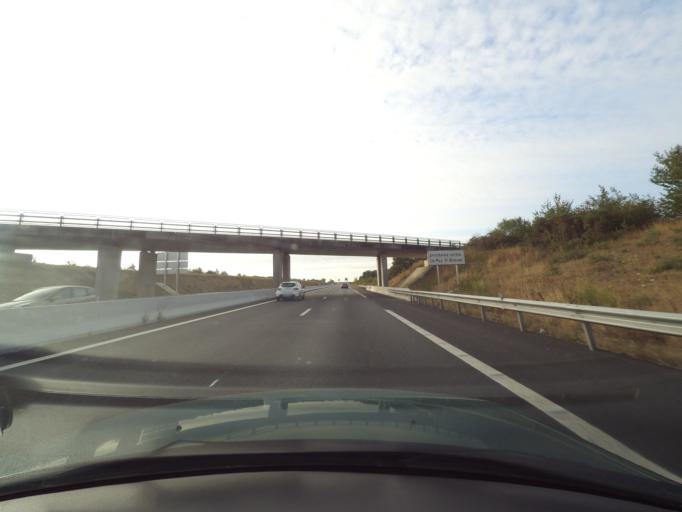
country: FR
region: Pays de la Loire
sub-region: Departement de Maine-et-Loire
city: Cholet
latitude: 47.0290
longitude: -0.8922
